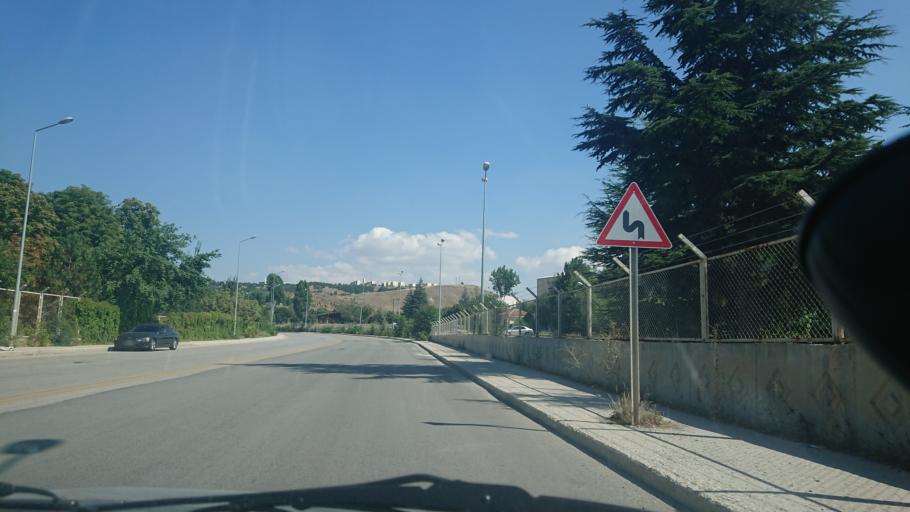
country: TR
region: Ankara
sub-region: Goelbasi
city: Golbasi
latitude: 39.8070
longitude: 32.8190
